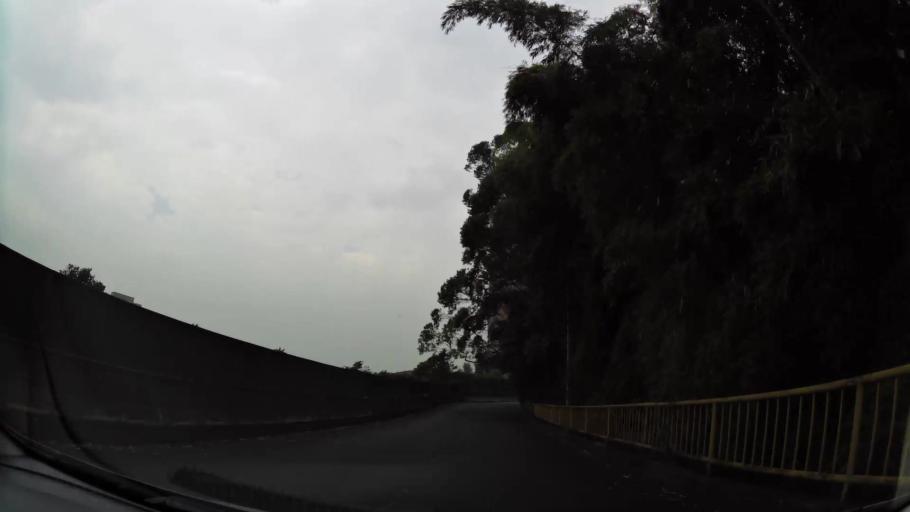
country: CO
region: Antioquia
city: Envigado
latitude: 6.2003
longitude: -75.5543
